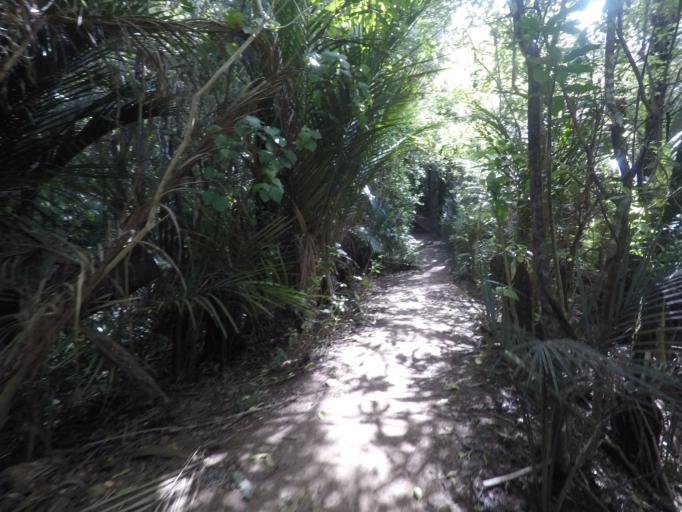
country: NZ
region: Auckland
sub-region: Auckland
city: Red Hill
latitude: -36.9855
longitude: 175.0380
